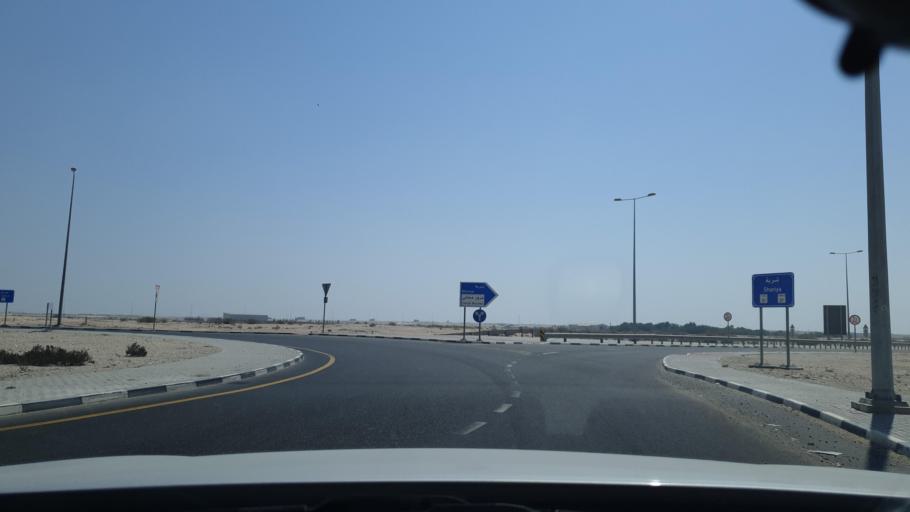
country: QA
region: Baladiyat Umm Salal
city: Umm Salal Muhammad
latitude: 25.3874
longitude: 51.3489
